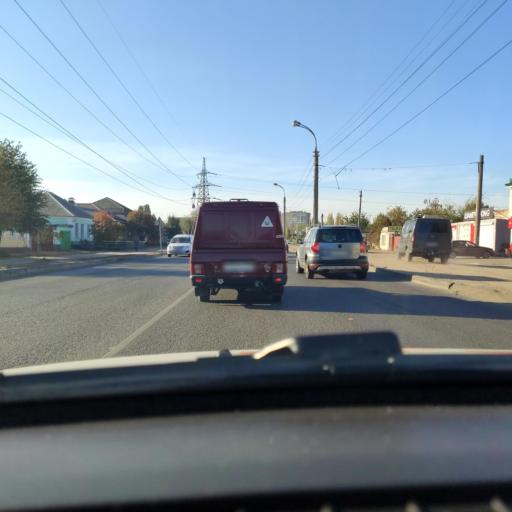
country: RU
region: Voronezj
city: Voronezh
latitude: 51.6429
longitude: 39.1565
